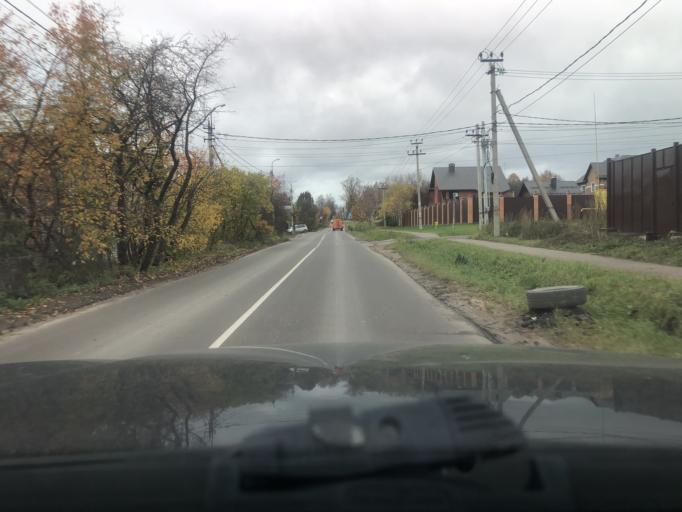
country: RU
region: Moskovskaya
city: Sergiyev Posad
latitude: 56.3033
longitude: 38.1099
